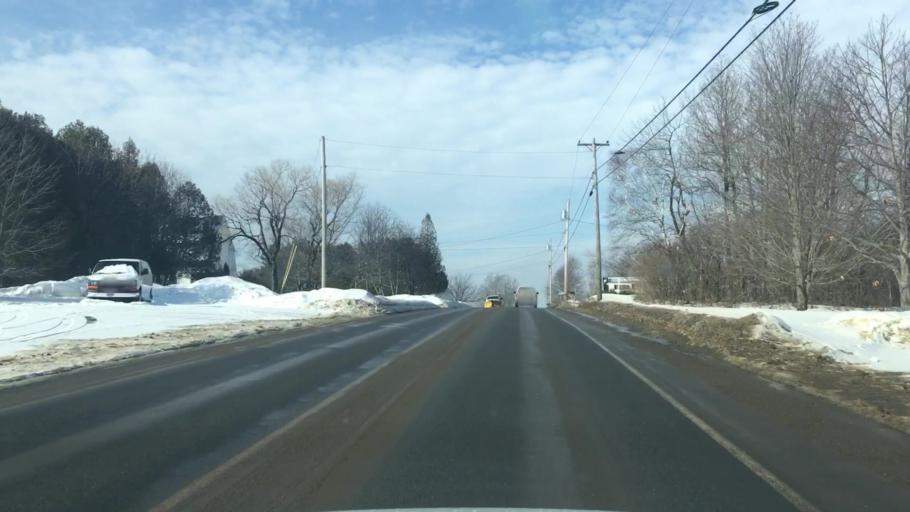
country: US
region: Maine
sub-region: Penobscot County
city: Hermon
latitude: 44.8458
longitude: -68.8692
